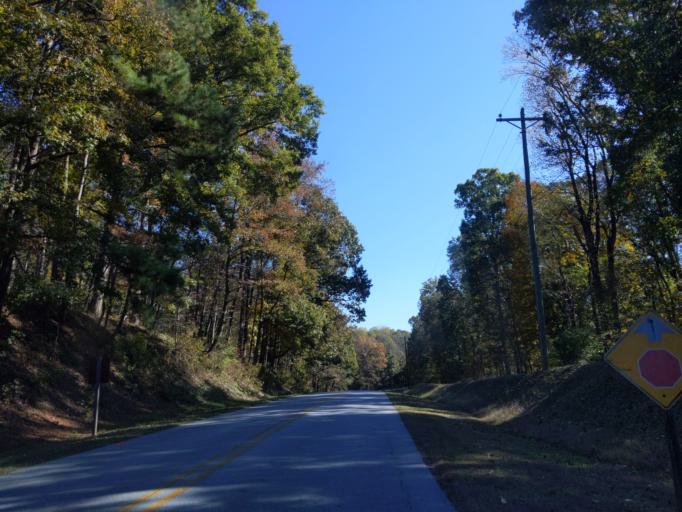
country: US
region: Georgia
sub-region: Franklin County
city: Gumlog
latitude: 34.4948
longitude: -83.0698
